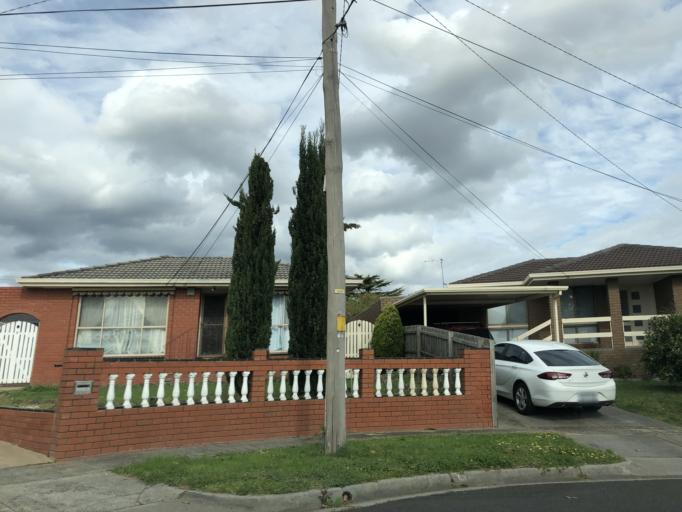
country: AU
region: Victoria
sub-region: Greater Dandenong
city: Noble Park North
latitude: -37.9476
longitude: 145.1965
